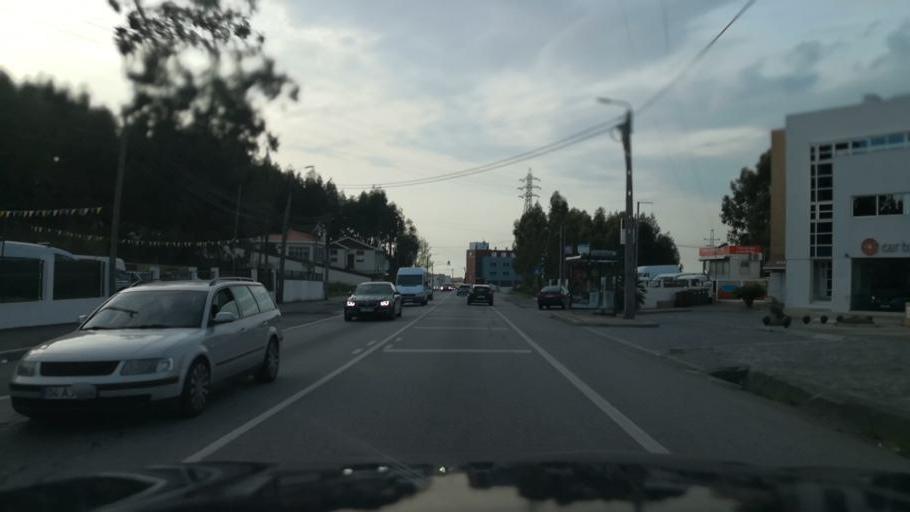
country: PT
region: Porto
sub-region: Gondomar
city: Baguim do Monte
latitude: 41.2056
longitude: -8.5292
